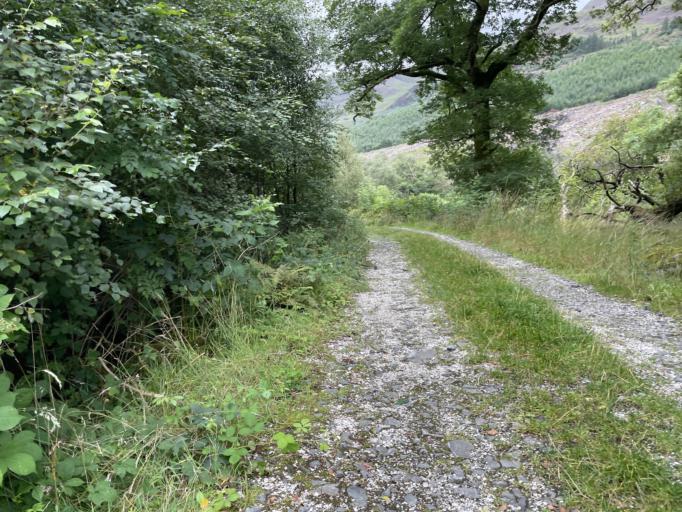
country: GB
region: Scotland
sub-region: Dumfries and Galloway
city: Newton Stewart
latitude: 55.0899
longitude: -4.4593
